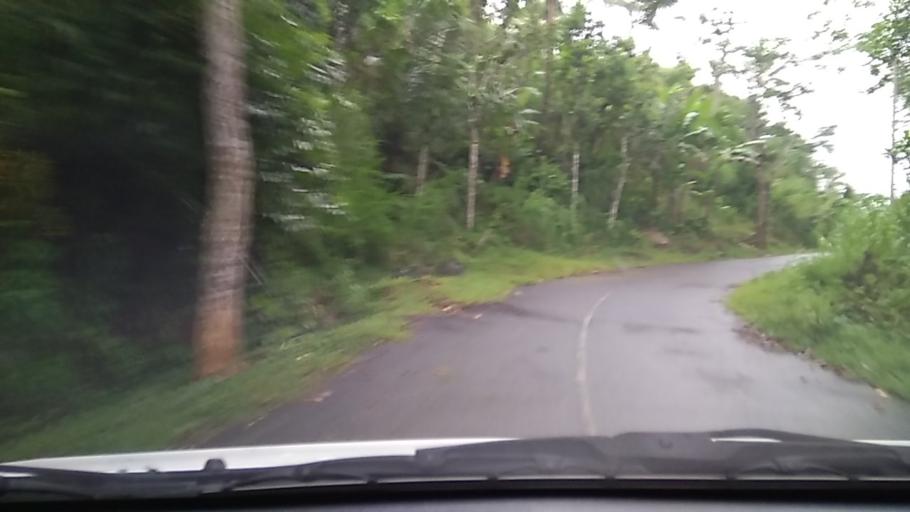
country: ID
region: Bali
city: Tistagede
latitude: -8.3905
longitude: 115.6266
